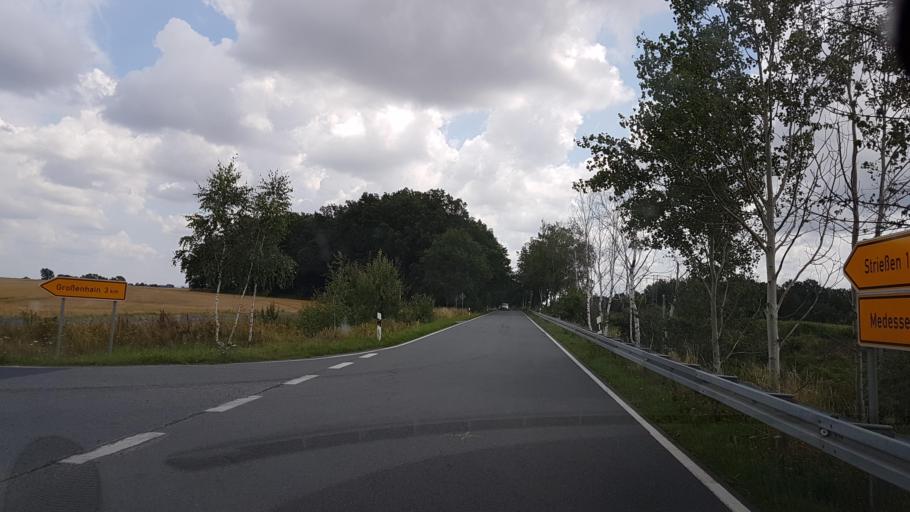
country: DE
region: Saxony
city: Weissig
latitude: 51.2680
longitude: 13.4713
